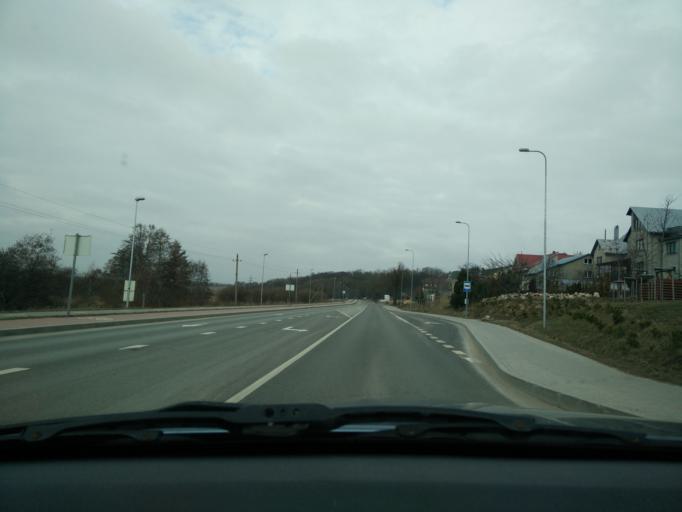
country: LT
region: Klaipedos apskritis
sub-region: Klaipeda
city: Klaipeda
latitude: 55.7183
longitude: 21.1690
